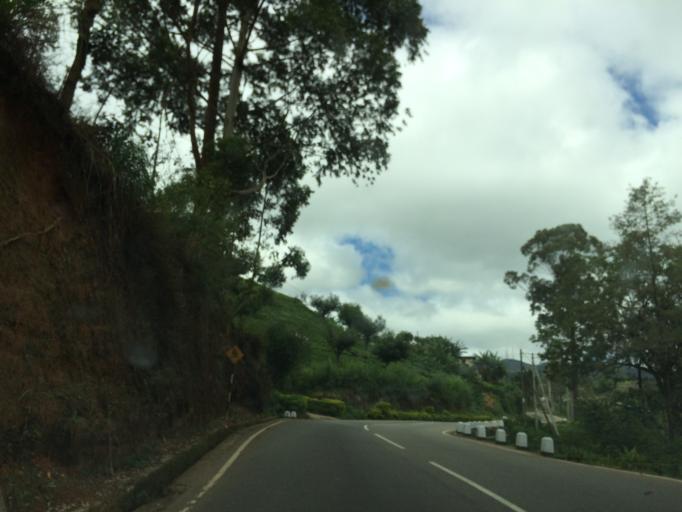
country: LK
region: Central
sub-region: Nuwara Eliya District
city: Nuwara Eliya
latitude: 7.0241
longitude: 80.7210
